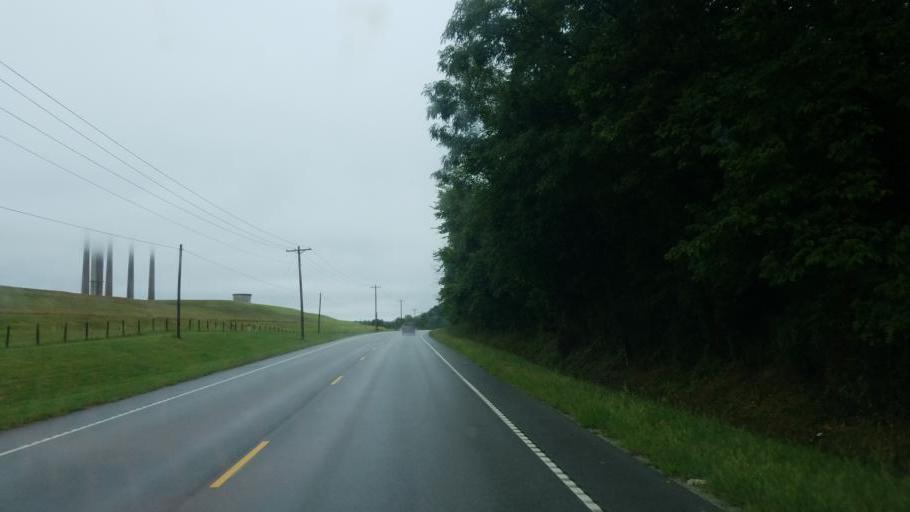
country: US
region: Kentucky
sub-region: Mason County
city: Maysville
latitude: 38.6390
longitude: -83.6732
